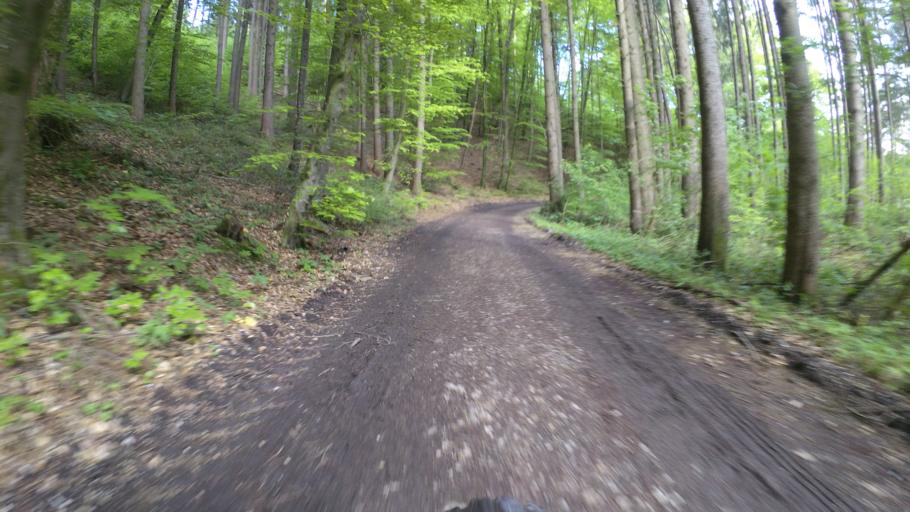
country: DE
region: Bavaria
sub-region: Upper Bavaria
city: Grabenstatt
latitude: 47.8476
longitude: 12.5698
